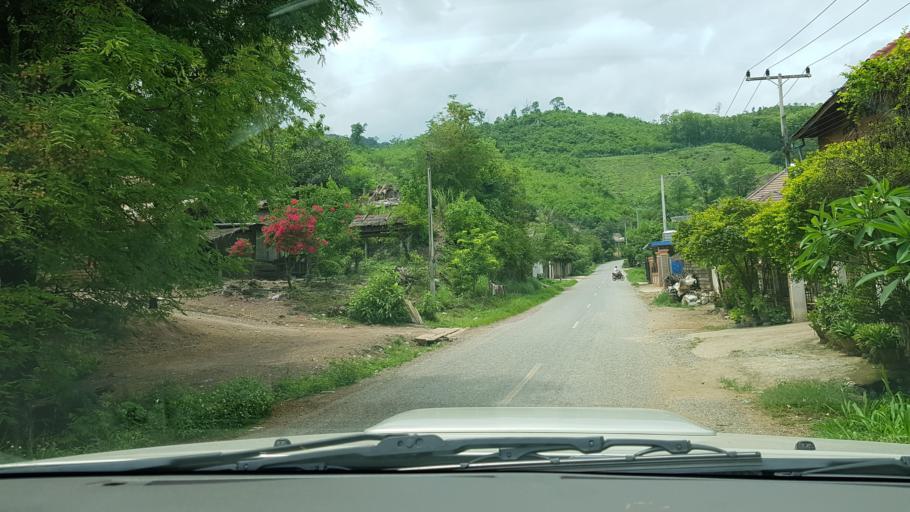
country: TH
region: Nan
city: Chaloem Phra Kiat
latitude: 19.9641
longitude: 101.2631
